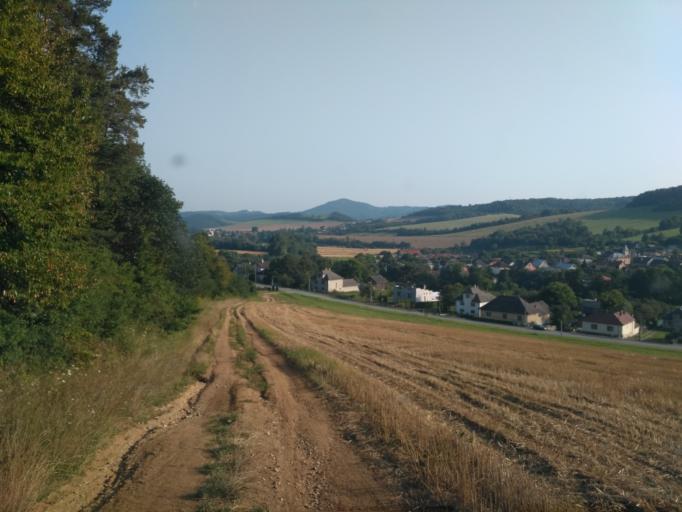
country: SK
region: Presovsky
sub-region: Okres Presov
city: Presov
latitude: 48.9436
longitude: 21.1802
